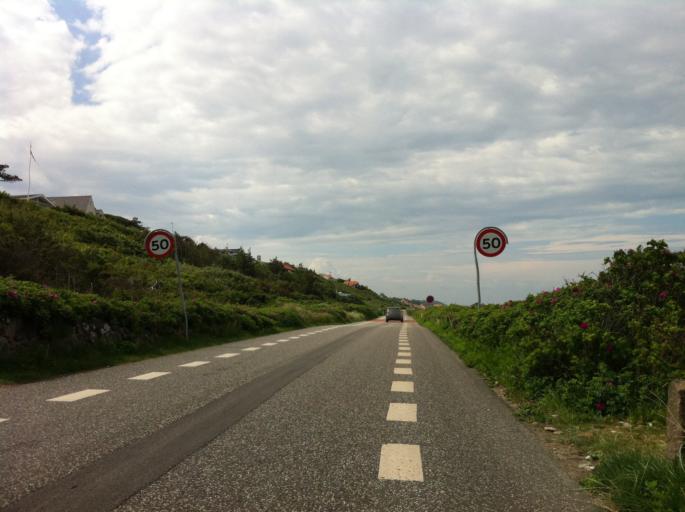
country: DK
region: Capital Region
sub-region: Gribskov Kommune
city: Helsinge
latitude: 56.1036
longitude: 12.1709
